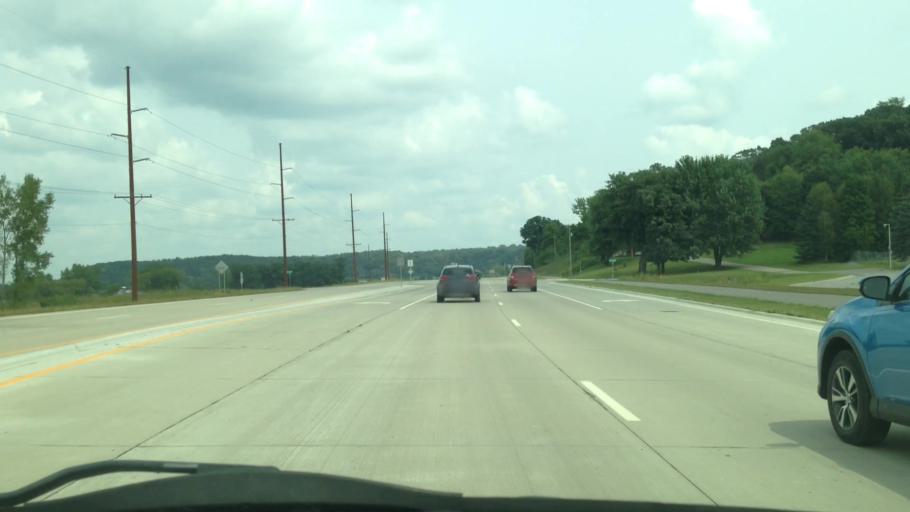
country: US
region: Minnesota
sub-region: Olmsted County
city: Rochester
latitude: 44.0638
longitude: -92.4519
